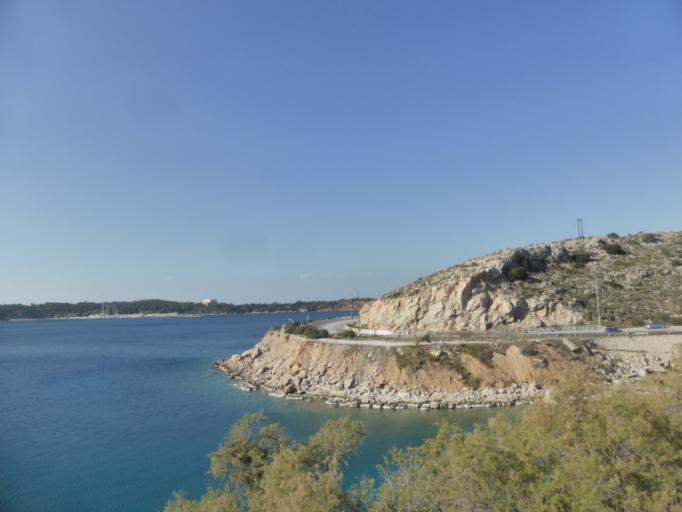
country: GR
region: Attica
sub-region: Nomarchia Anatolikis Attikis
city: Vouliagmeni
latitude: 37.8020
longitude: 23.7871
